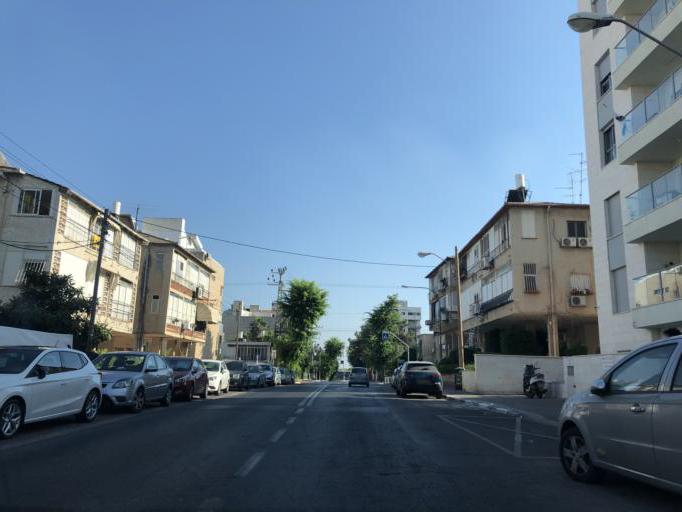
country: IL
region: Tel Aviv
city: Giv`atayim
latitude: 32.0690
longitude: 34.8245
